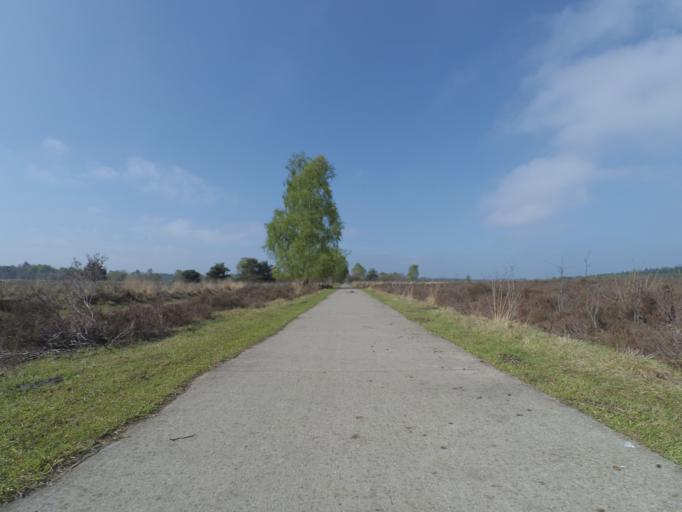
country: NL
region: Gelderland
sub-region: Gemeente Apeldoorn
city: Uddel
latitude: 52.2876
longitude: 5.7715
